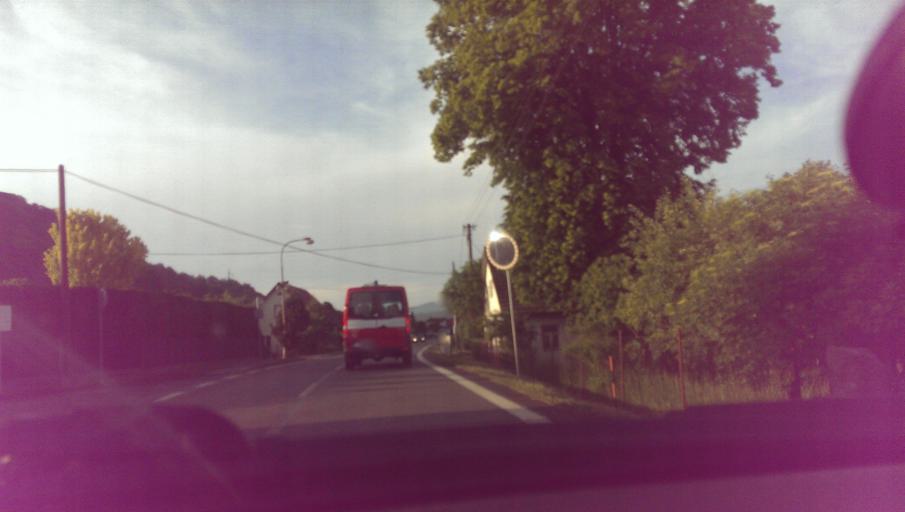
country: CZ
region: Zlin
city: Valasska Polanka
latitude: 49.2882
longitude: 17.9983
